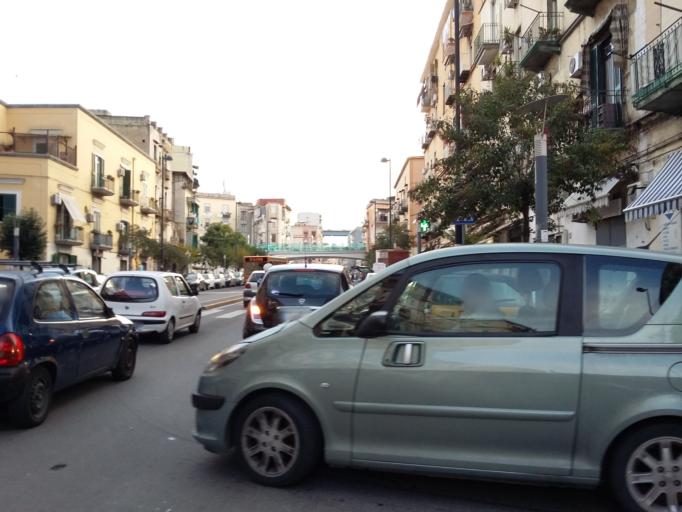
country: IT
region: Campania
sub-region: Provincia di Napoli
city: Napoli
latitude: 40.8636
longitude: 14.2698
